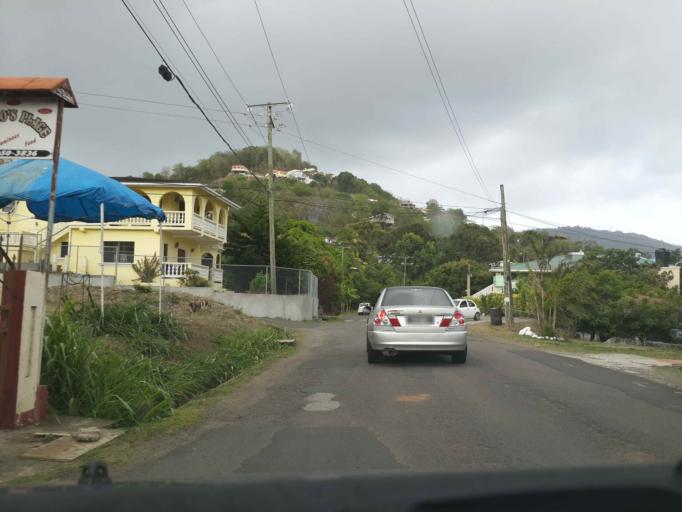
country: LC
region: Gros-Islet
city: Gros Islet
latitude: 14.0446
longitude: -60.9579
